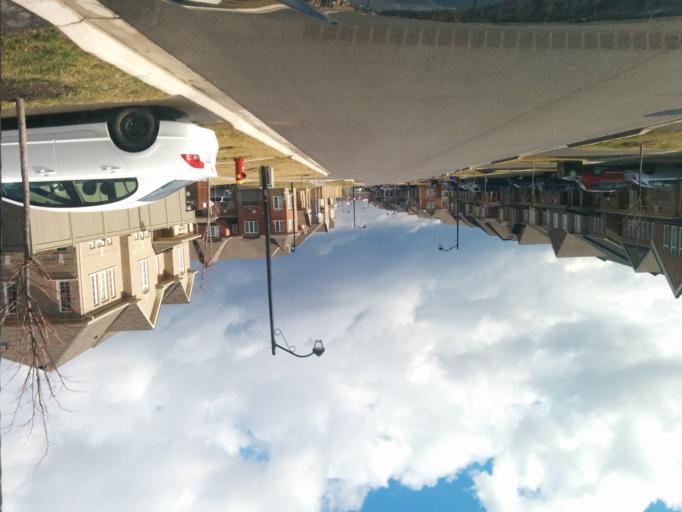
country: CA
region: Ontario
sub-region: Halton
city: Milton
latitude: 43.4927
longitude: -79.8699
